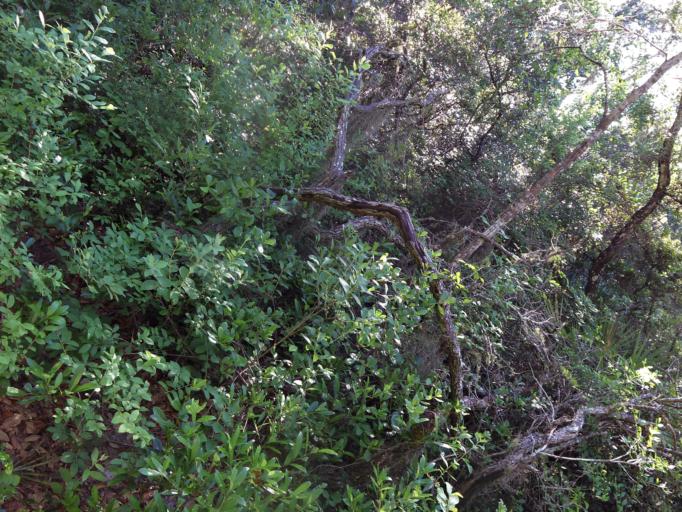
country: US
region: Florida
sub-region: Duval County
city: Atlantic Beach
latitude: 30.3805
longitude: -81.4865
